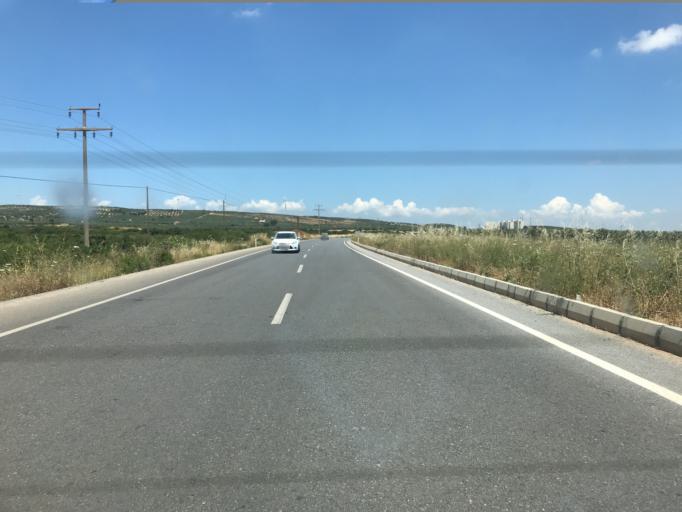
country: TR
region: Aydin
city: Akkoy
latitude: 37.4616
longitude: 27.3394
